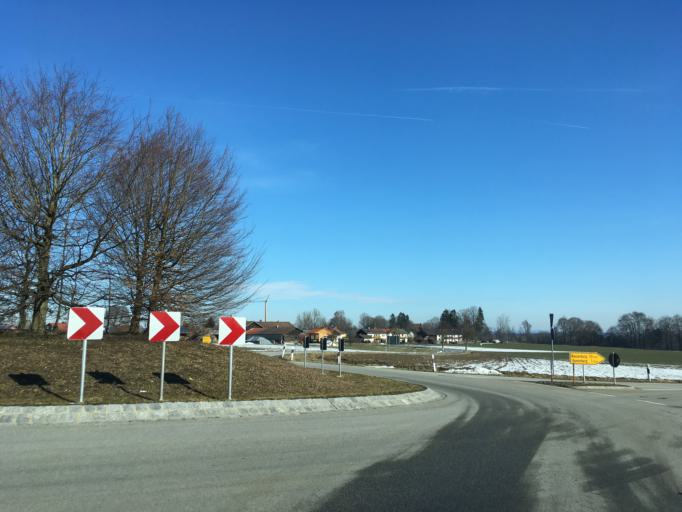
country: DE
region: Bavaria
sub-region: Upper Bavaria
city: Ramerberg
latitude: 48.0228
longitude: 12.1394
